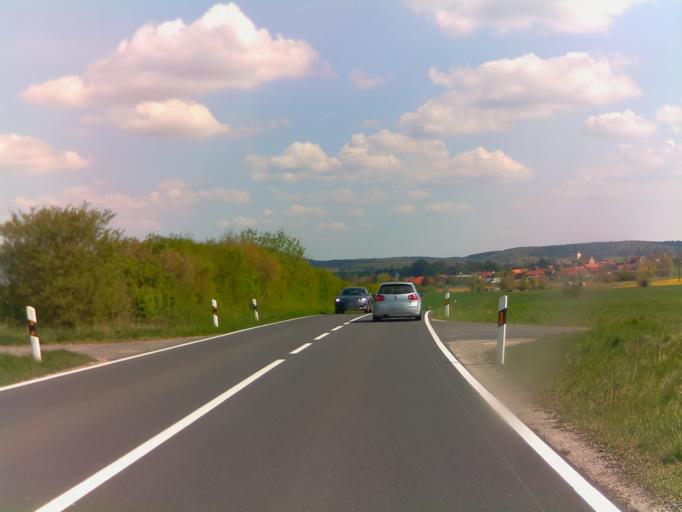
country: DE
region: Thuringia
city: Westhausen
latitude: 50.3635
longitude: 10.6722
